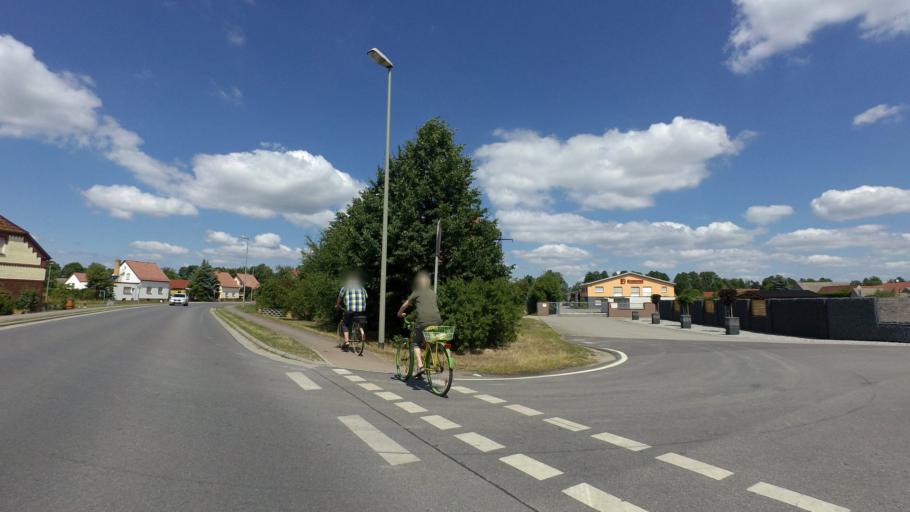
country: DE
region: Brandenburg
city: Sonnewalde
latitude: 51.6651
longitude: 13.6454
